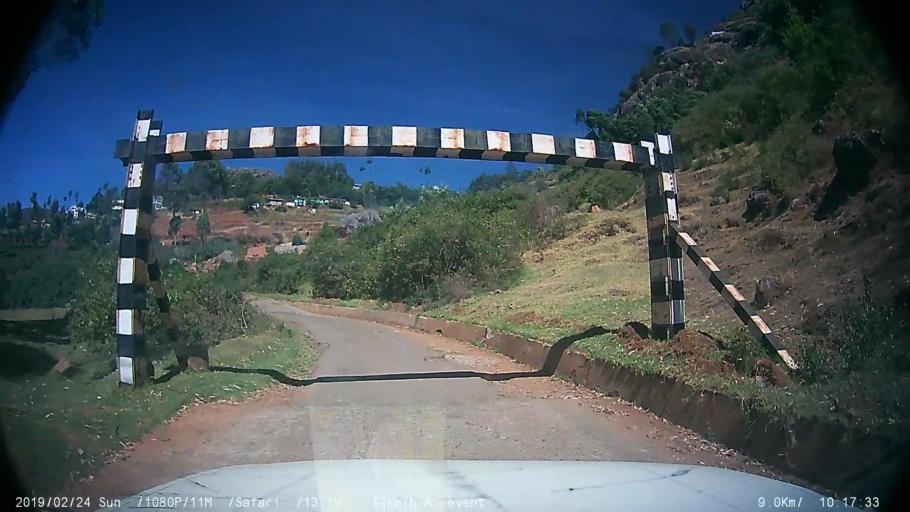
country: IN
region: Tamil Nadu
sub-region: Nilgiri
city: Ooty
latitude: 11.3869
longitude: 76.7221
